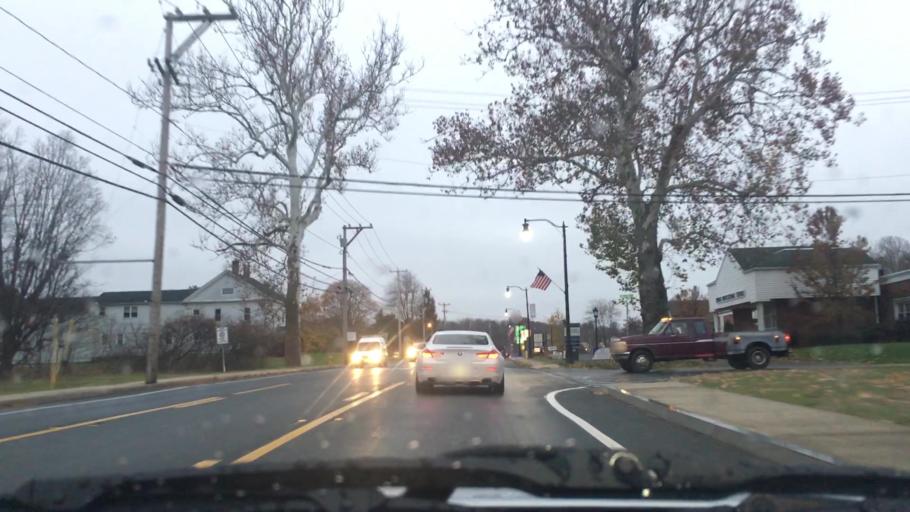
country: US
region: Massachusetts
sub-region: Hampden County
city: Southwick
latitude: 42.0658
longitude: -72.7642
